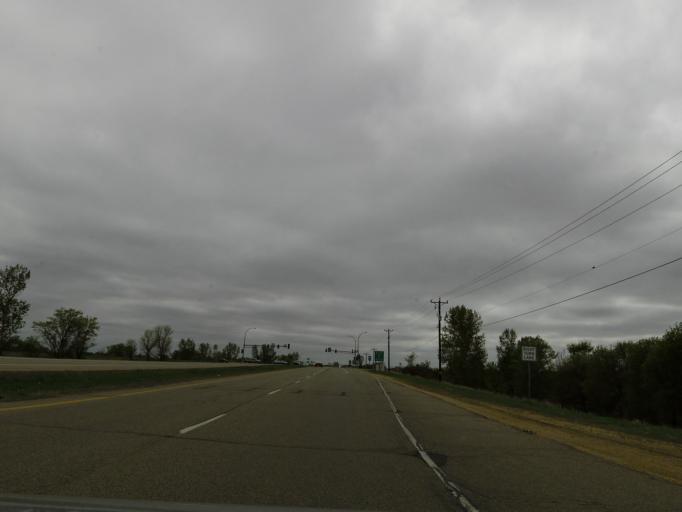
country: US
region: Minnesota
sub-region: Washington County
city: Lake Elmo
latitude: 44.9514
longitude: -92.8628
